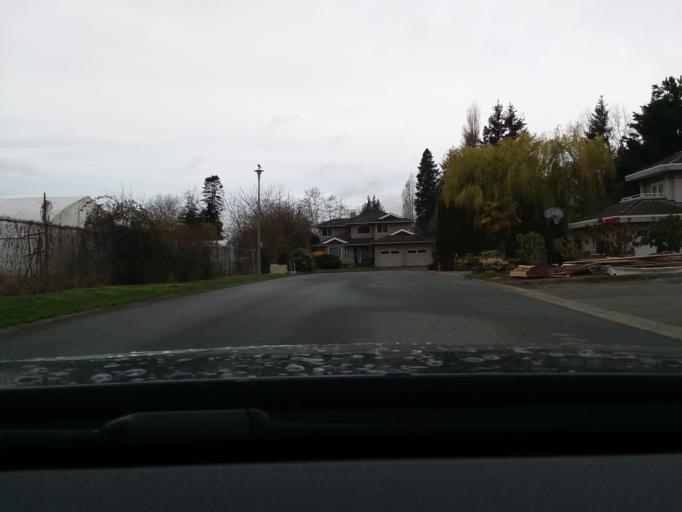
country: CA
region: British Columbia
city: Victoria
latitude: 48.5133
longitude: -123.3781
